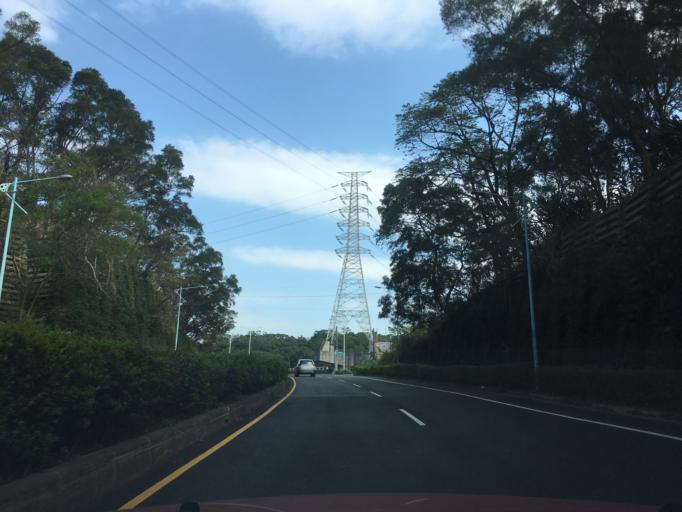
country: TW
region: Taiwan
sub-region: Hsinchu
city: Hsinchu
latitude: 24.7627
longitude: 121.0079
